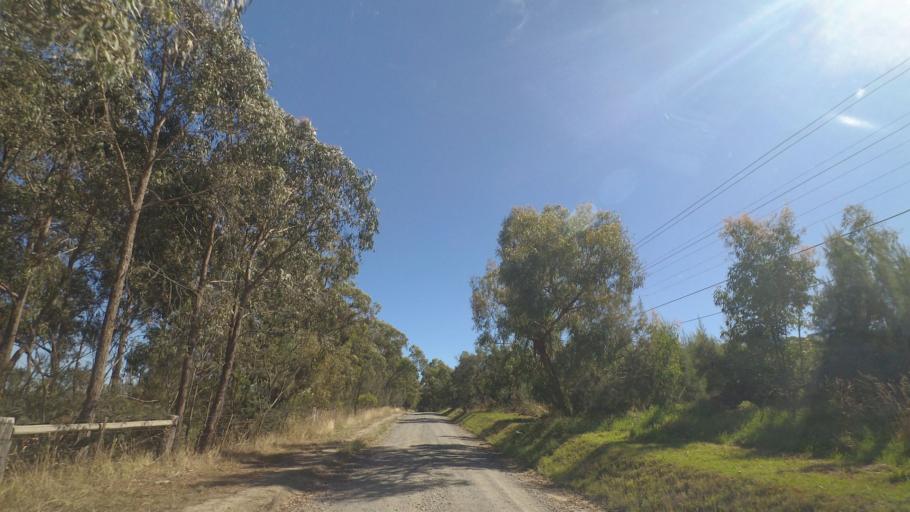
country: AU
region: Victoria
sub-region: Knox
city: Wantirna South
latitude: -37.8717
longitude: 145.2000
